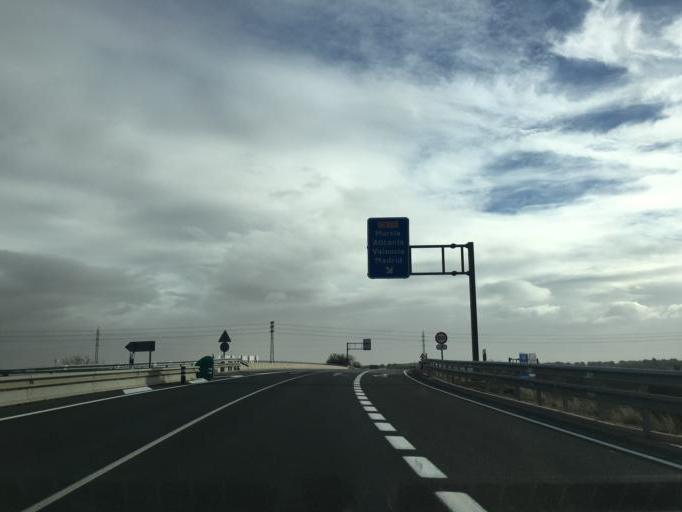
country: ES
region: Castille-La Mancha
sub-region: Provincia de Albacete
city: Albacete
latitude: 39.0025
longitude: -1.9041
